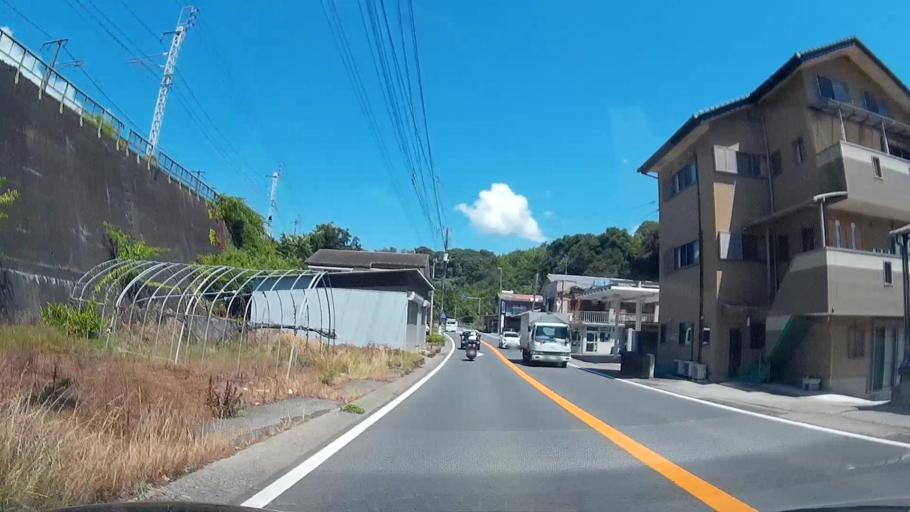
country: JP
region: Gunma
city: Numata
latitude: 36.6193
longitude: 139.0409
